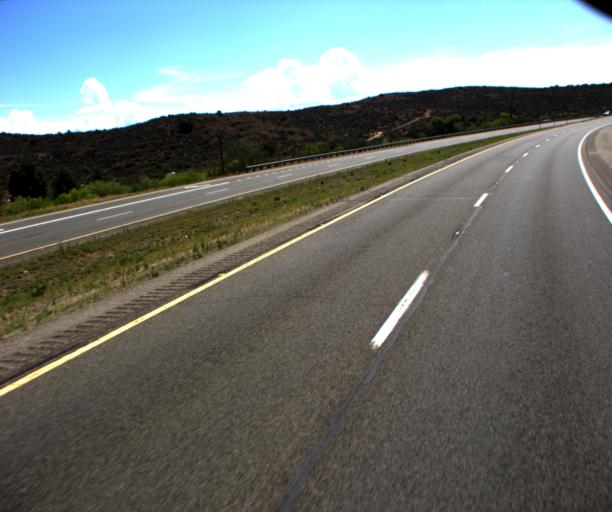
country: US
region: Arizona
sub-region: Yavapai County
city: Mayer
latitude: 34.3808
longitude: -112.1977
